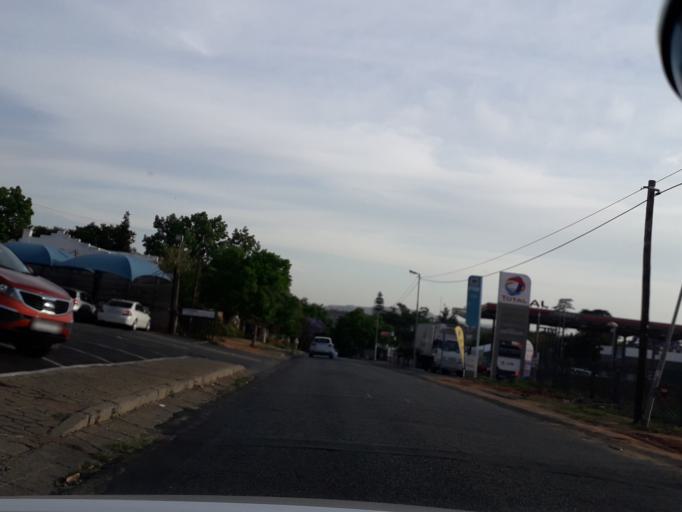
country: ZA
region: Gauteng
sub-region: City of Johannesburg Metropolitan Municipality
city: Johannesburg
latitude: -26.0758
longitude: 27.9905
